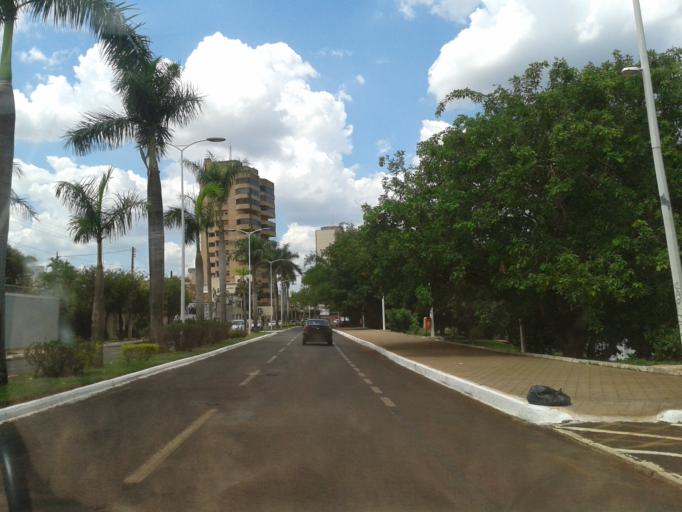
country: BR
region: Goias
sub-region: Itumbiara
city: Itumbiara
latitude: -18.4147
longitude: -49.2121
